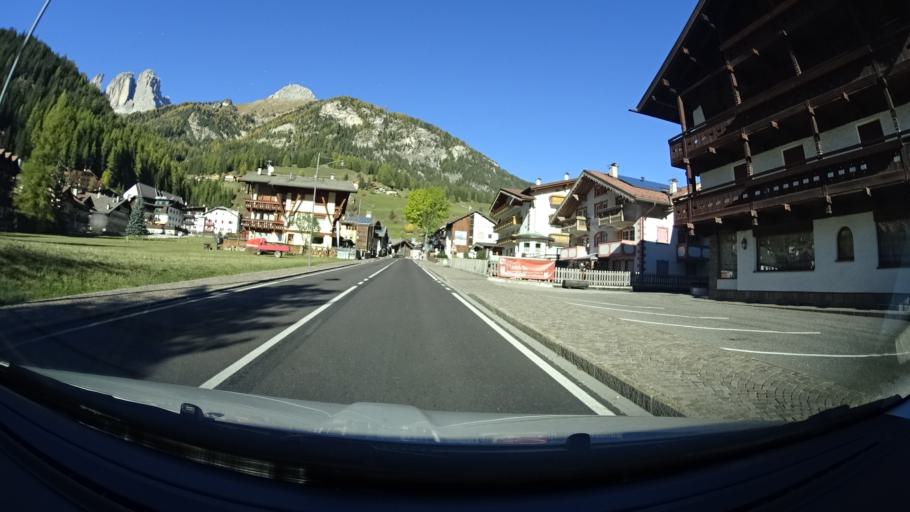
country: IT
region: Trentino-Alto Adige
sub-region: Provincia di Trento
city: Campitello di Fassa
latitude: 46.4751
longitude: 11.7390
